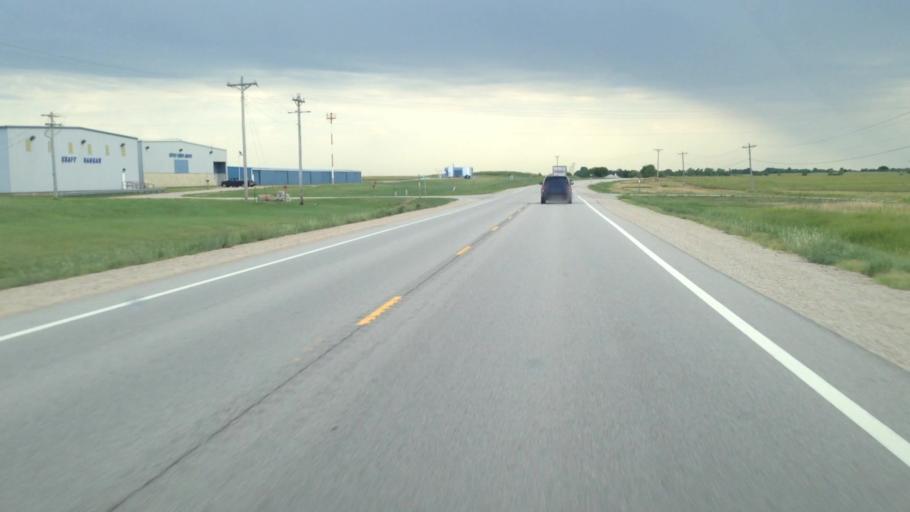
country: US
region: Kansas
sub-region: Coffey County
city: Burlington
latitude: 38.3042
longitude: -95.7288
